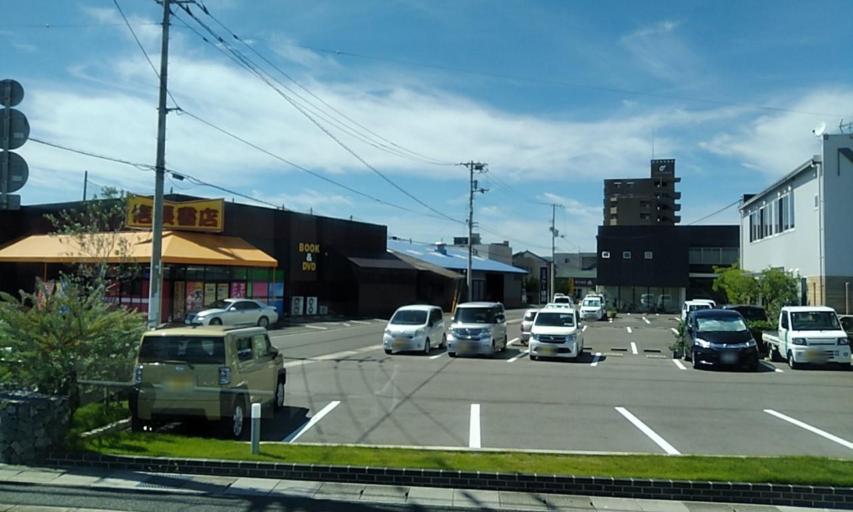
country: JP
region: Kagawa
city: Takamatsu-shi
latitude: 34.3120
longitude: 134.0708
